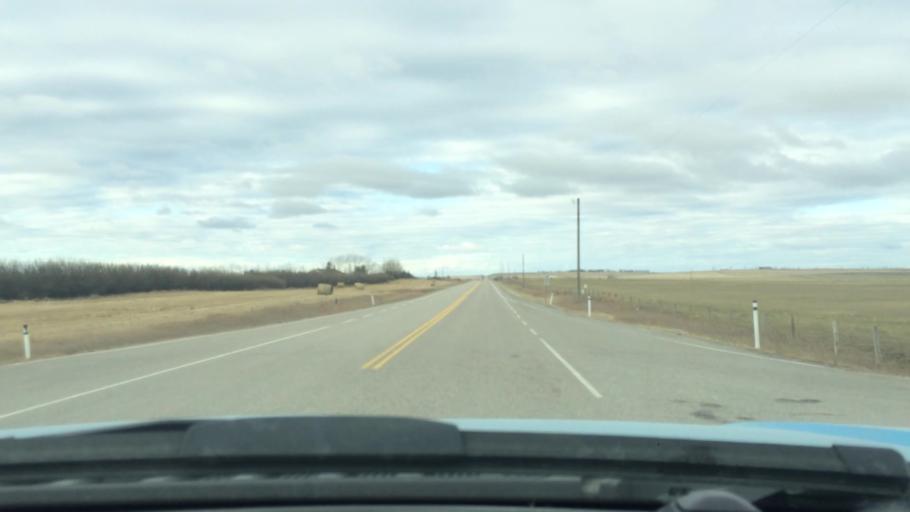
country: CA
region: Alberta
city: Airdrie
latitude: 51.2124
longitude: -114.0712
